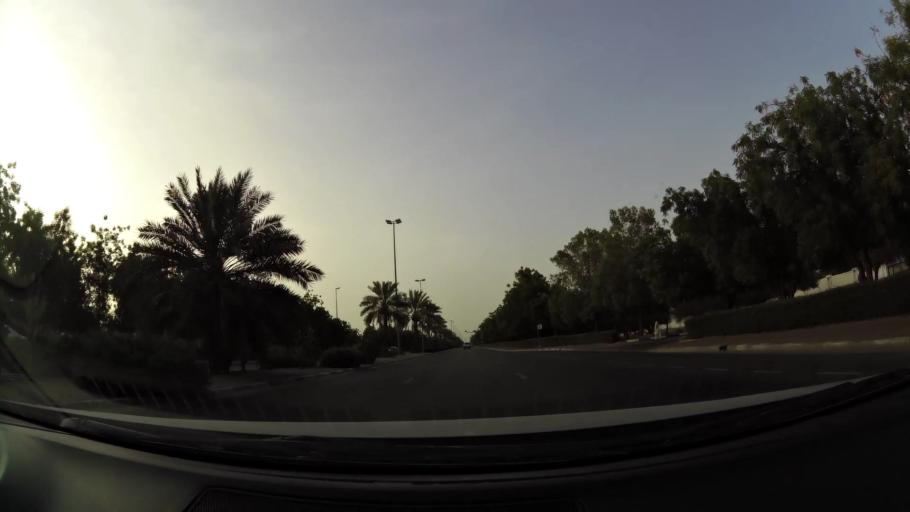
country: AE
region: Abu Dhabi
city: Al Ain
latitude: 24.2512
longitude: 55.7199
